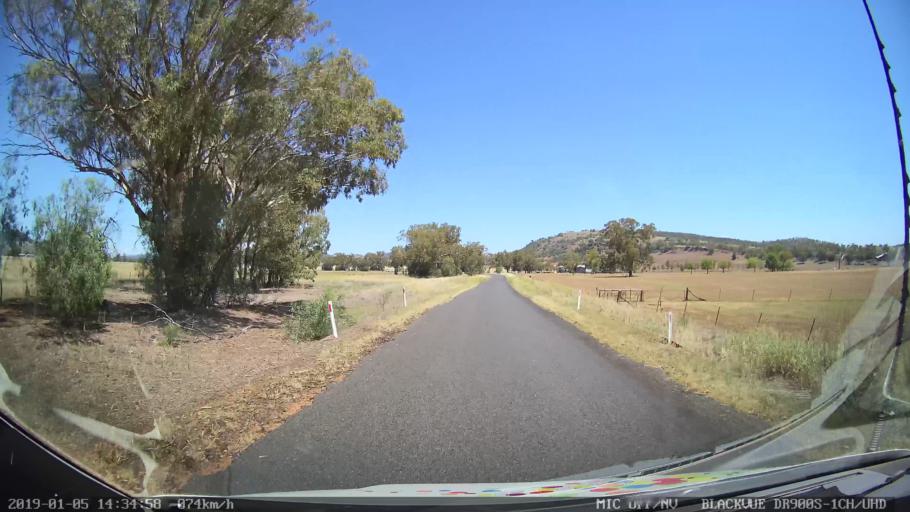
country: AU
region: New South Wales
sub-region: Tamworth Municipality
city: Phillip
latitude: -31.2373
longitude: 150.6464
